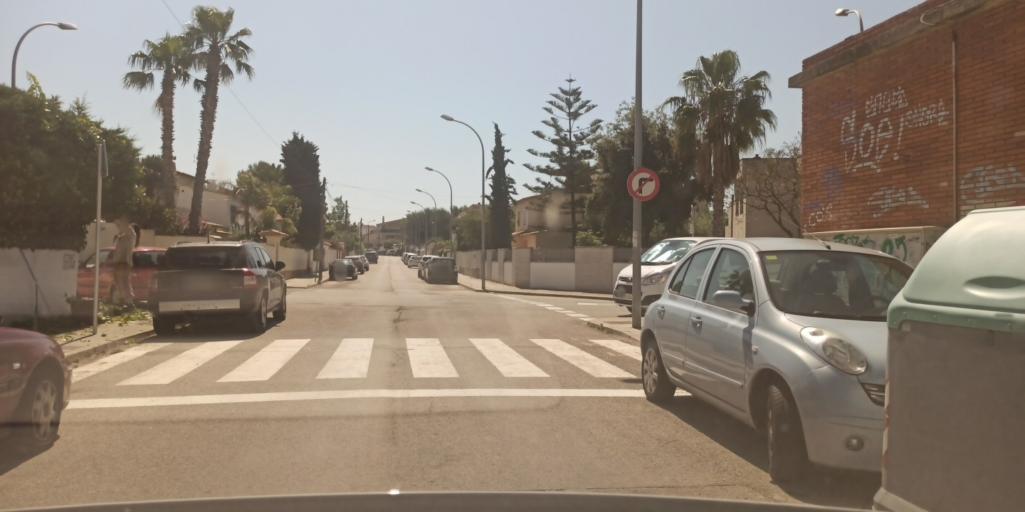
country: ES
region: Catalonia
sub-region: Provincia de Barcelona
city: Sant Pere de Ribes
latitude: 41.2591
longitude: 1.7664
